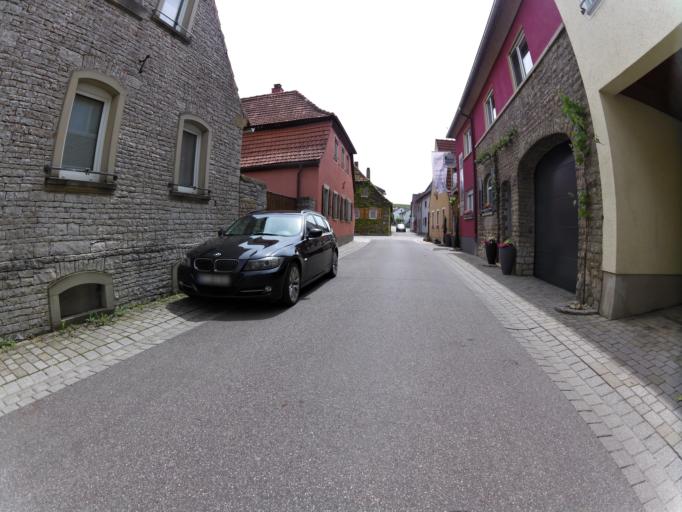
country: DE
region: Bavaria
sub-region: Regierungsbezirk Unterfranken
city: Nordheim
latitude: 49.8597
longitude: 10.1855
